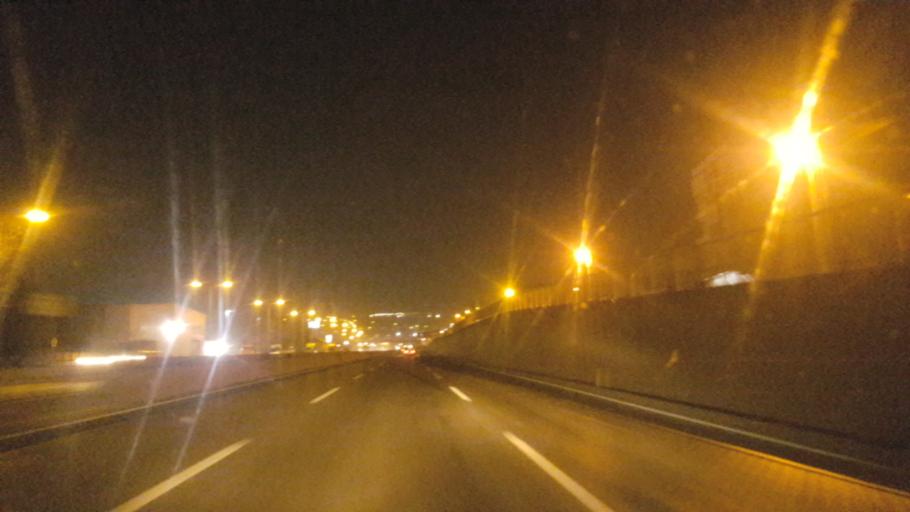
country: TR
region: Kocaeli
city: Tavsancil
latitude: 40.7846
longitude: 29.5362
